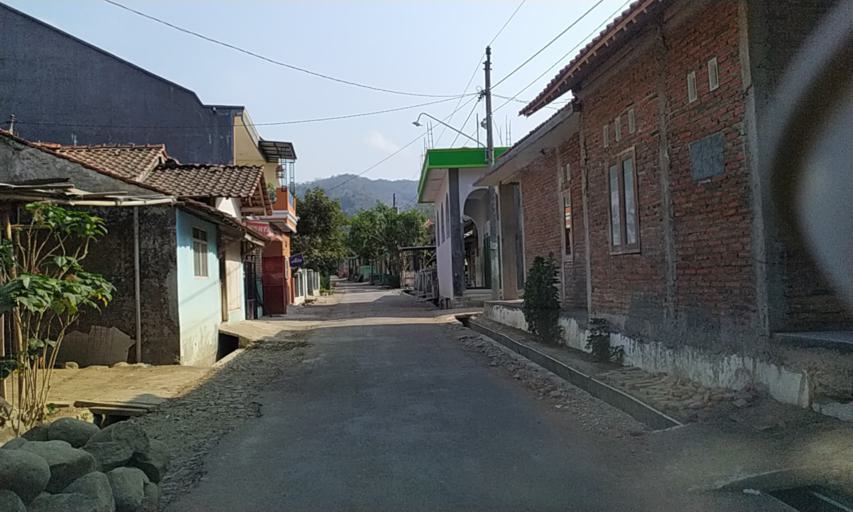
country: ID
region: Central Java
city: Jambuluwuk
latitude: -7.3200
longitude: 108.8787
